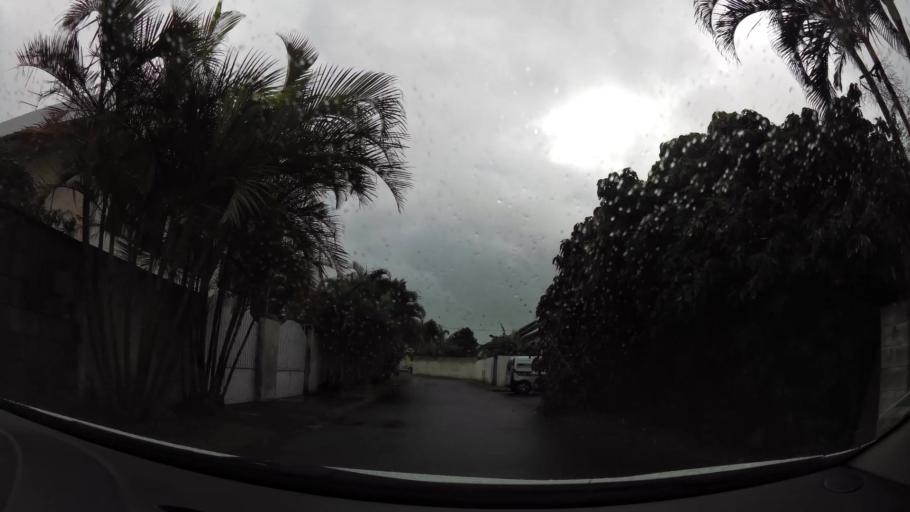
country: RE
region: Reunion
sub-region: Reunion
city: Saint-Andre
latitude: -20.9545
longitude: 55.6556
